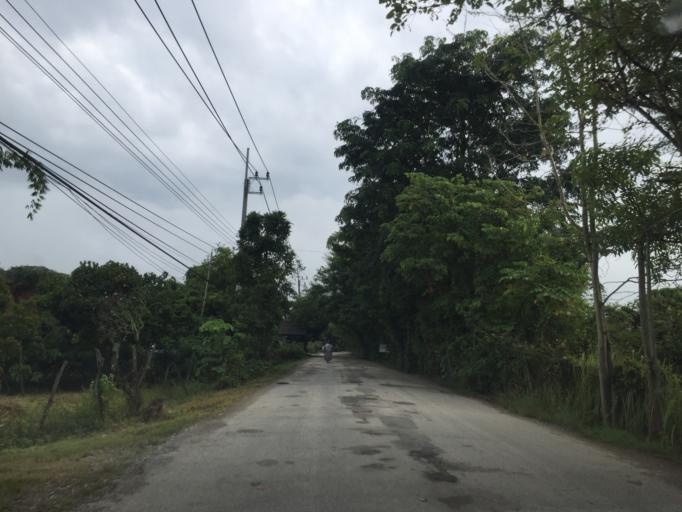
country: TH
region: Lamphun
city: Ban Thi
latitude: 18.6583
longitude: 99.0708
